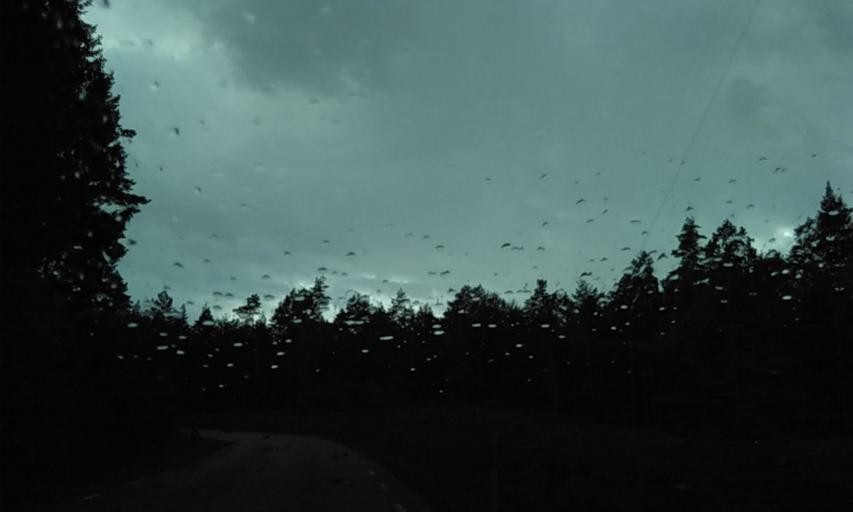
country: SE
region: Vaestra Goetaland
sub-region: Grastorps Kommun
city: Graestorp
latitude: 58.4553
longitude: 12.7921
